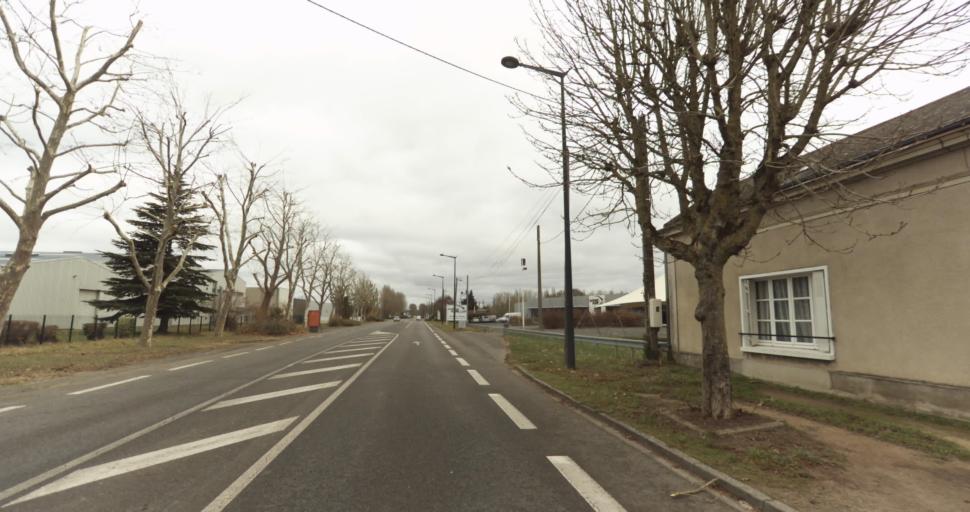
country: FR
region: Pays de la Loire
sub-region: Departement de Maine-et-Loire
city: Saumur
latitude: 47.2768
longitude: -0.0588
